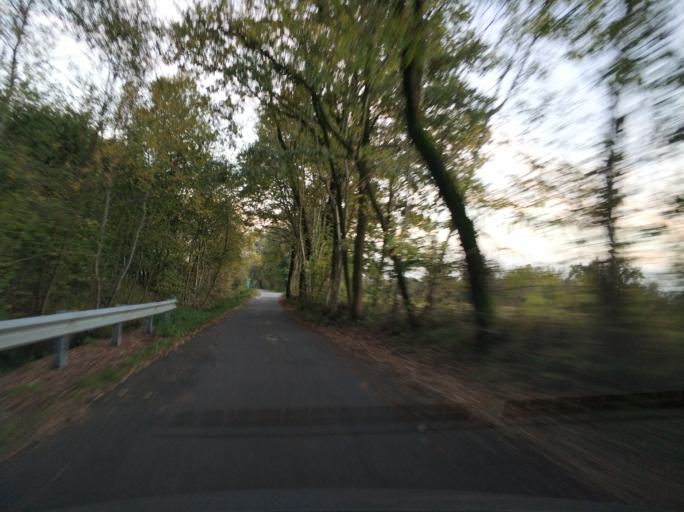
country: IT
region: Piedmont
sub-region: Provincia di Torino
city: Robassomero
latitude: 45.1867
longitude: 7.5823
